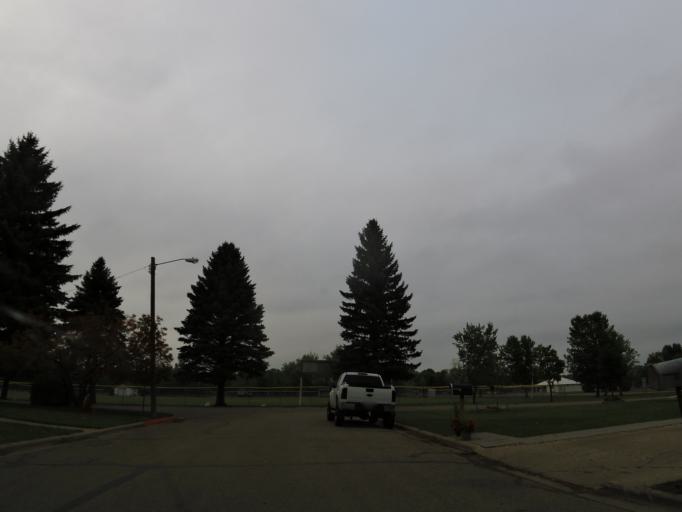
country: US
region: North Dakota
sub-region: Walsh County
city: Grafton
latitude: 48.5638
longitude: -97.1834
